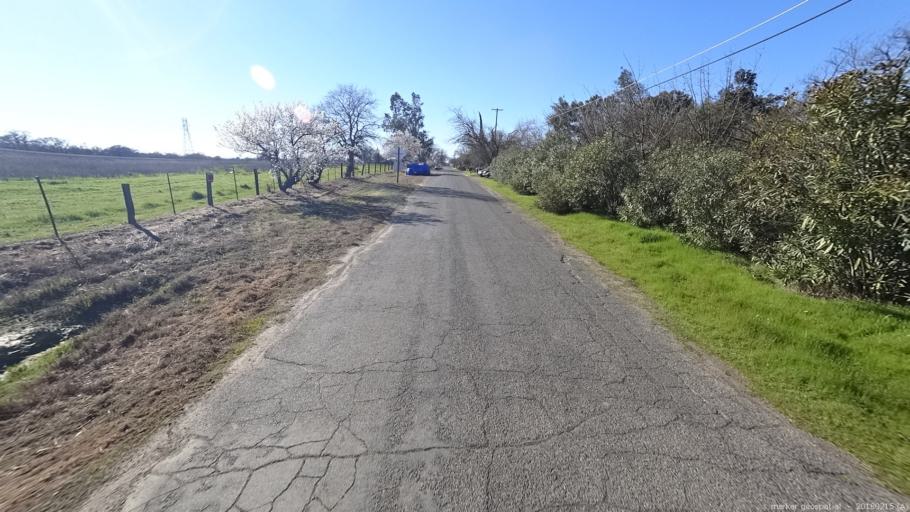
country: US
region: California
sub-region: Sacramento County
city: Rio Linda
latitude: 38.6694
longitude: -121.4588
